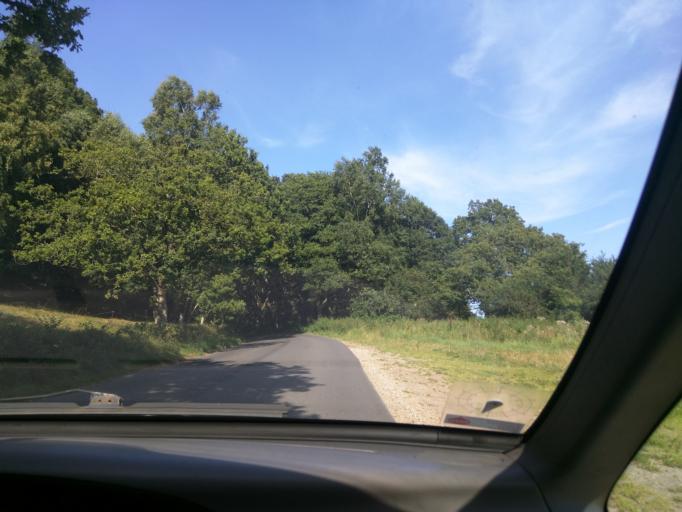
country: DK
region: Central Jutland
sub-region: Viborg Kommune
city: Bjerringbro
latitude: 56.4657
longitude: 9.6202
